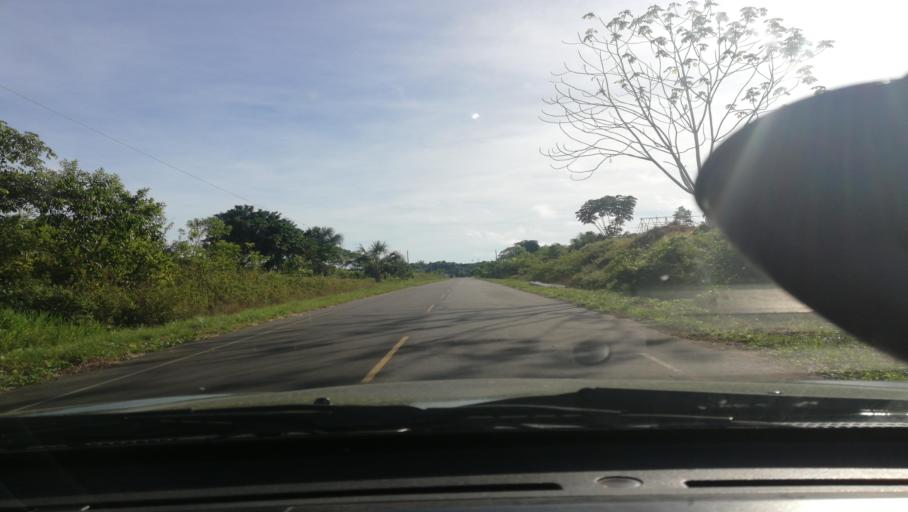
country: PE
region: Loreto
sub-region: Provincia de Loreto
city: Nauta
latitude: -4.3342
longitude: -73.5348
